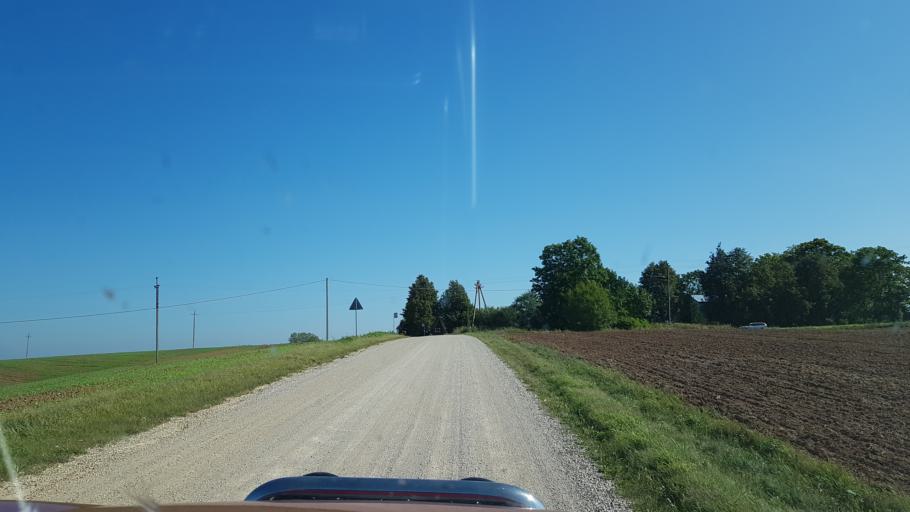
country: EE
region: Tartu
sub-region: UElenurme vald
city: Ulenurme
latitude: 58.2521
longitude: 26.8793
